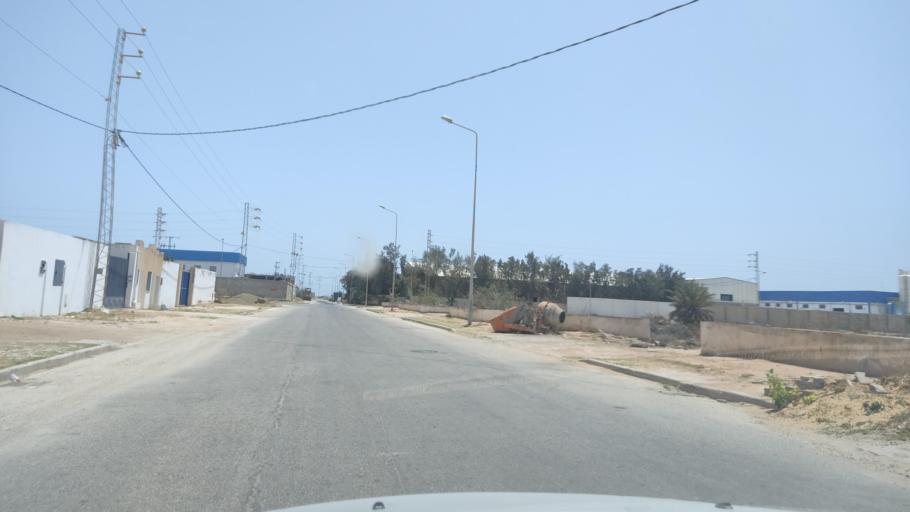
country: TN
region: Safaqis
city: Sfax
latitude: 34.6625
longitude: 10.6973
